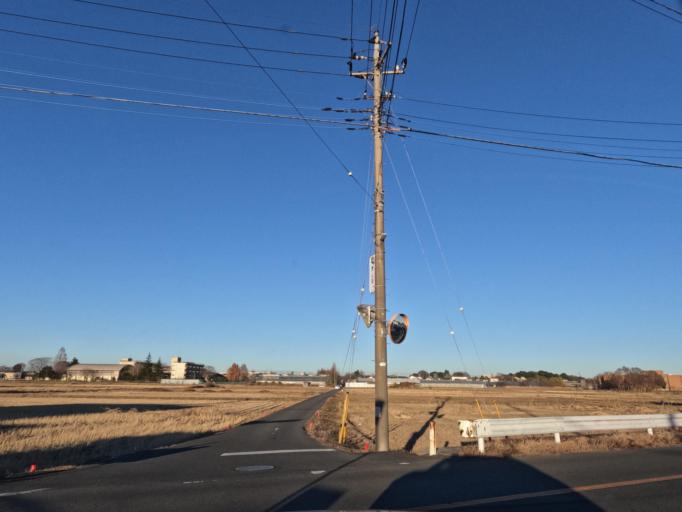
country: JP
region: Saitama
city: Hasuda
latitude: 35.9656
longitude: 139.6481
